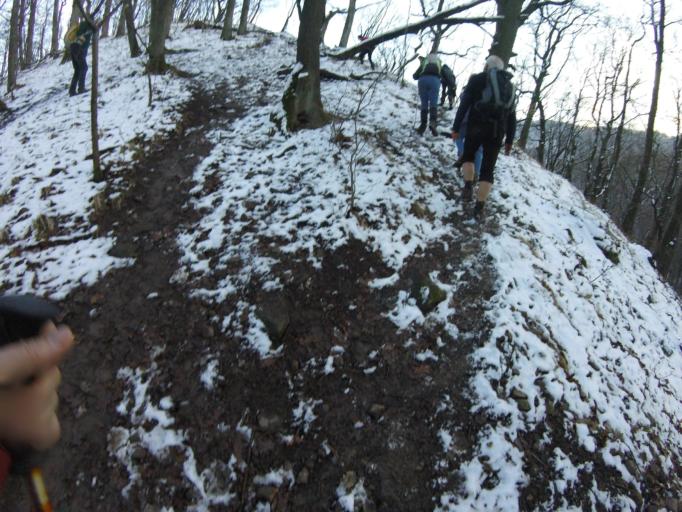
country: HU
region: Pest
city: Pilisszentkereszt
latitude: 47.7310
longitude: 18.8964
